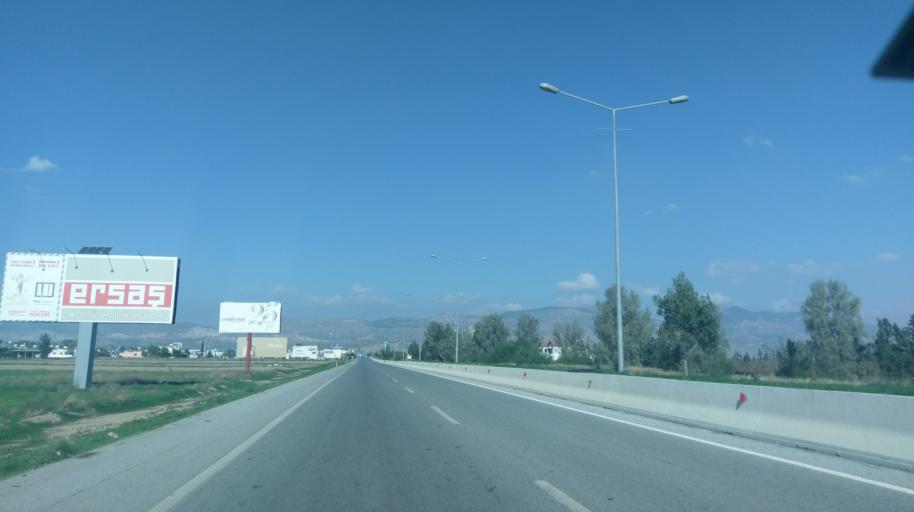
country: CY
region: Lefkosia
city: Geri
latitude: 35.2025
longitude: 33.4997
